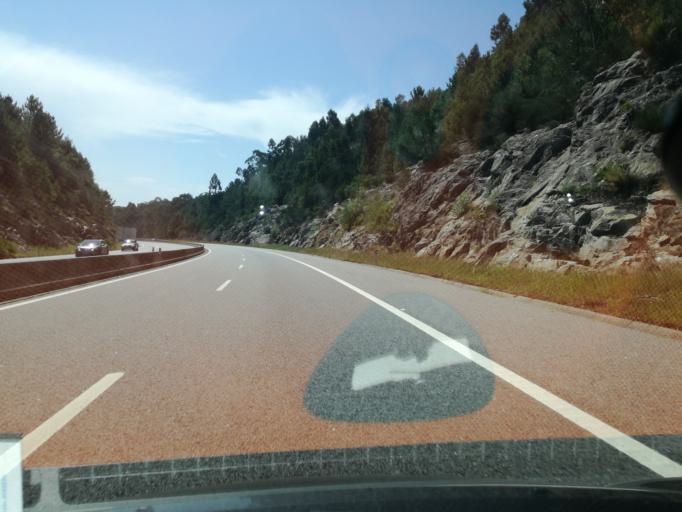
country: PT
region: Viana do Castelo
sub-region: Viana do Castelo
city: Meadela
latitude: 41.7485
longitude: -8.8000
